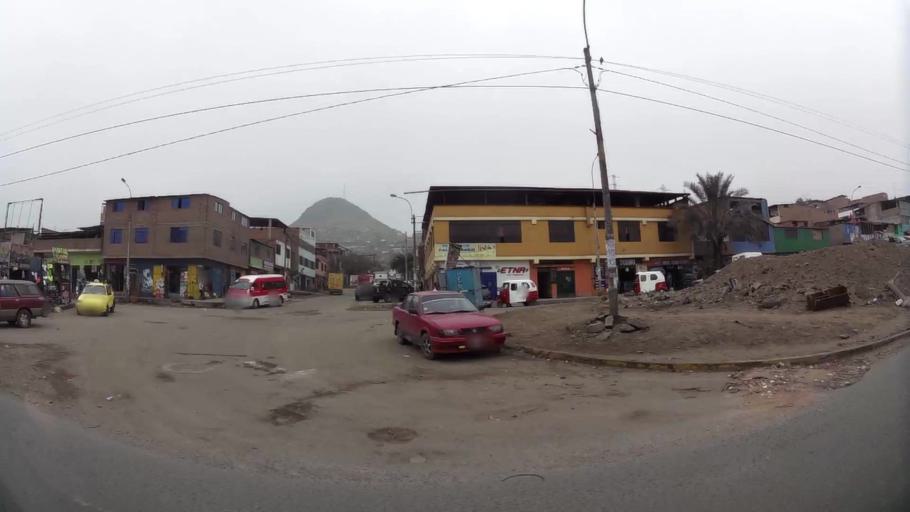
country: PE
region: Lima
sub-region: Lima
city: Surco
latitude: -12.1778
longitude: -76.9462
